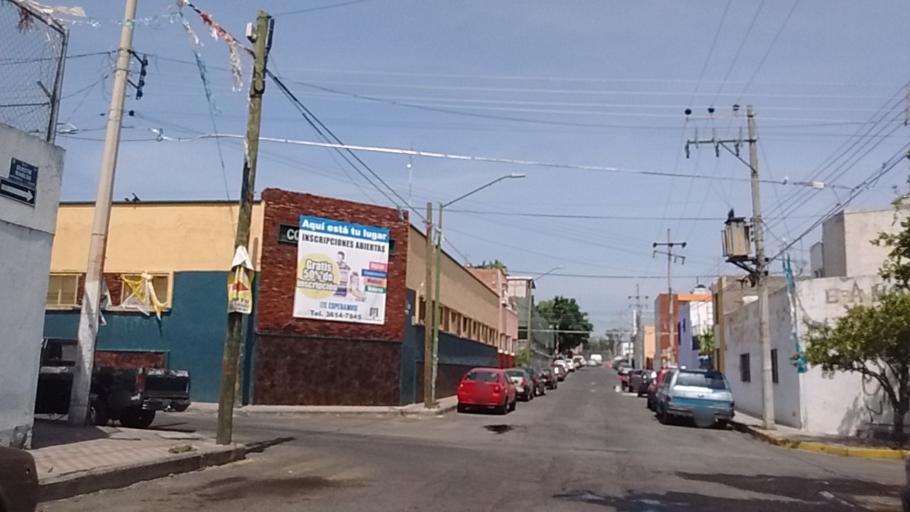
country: MX
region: Jalisco
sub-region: Zapopan
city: Zapopan
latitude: 20.6914
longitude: -103.3456
